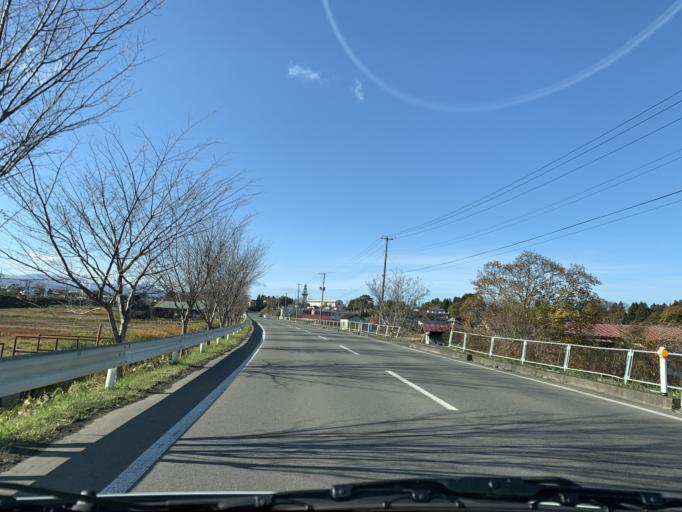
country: JP
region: Iwate
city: Mizusawa
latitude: 39.1910
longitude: 141.1235
